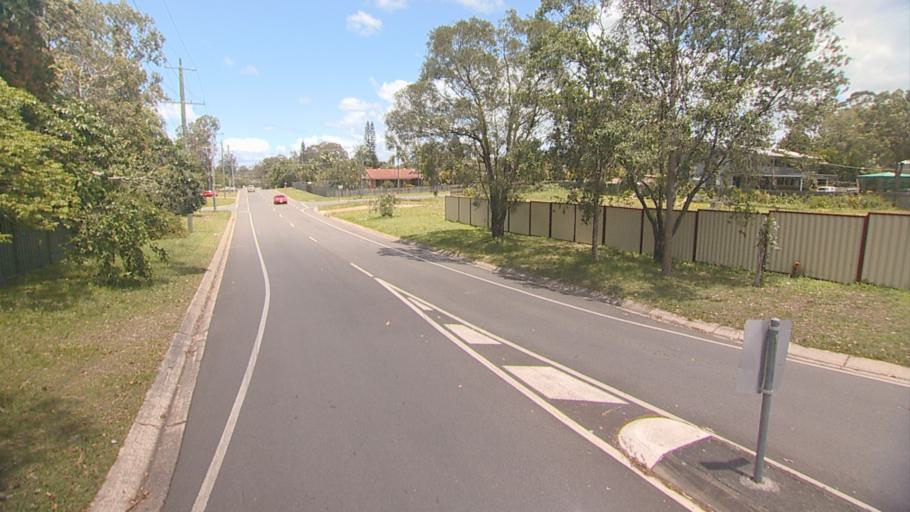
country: AU
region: Queensland
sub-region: Logan
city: Beenleigh
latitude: -27.6978
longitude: 153.2057
